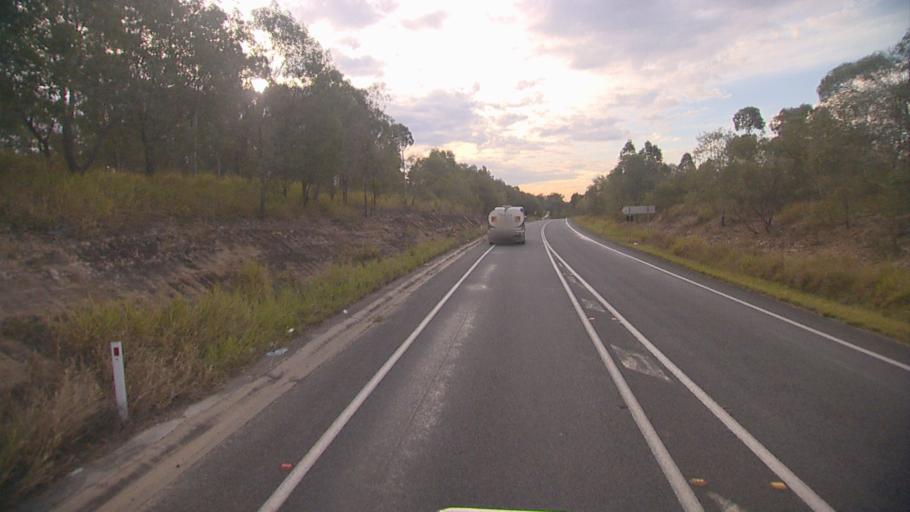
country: AU
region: Queensland
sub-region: Logan
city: Chambers Flat
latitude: -27.8351
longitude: 153.1075
